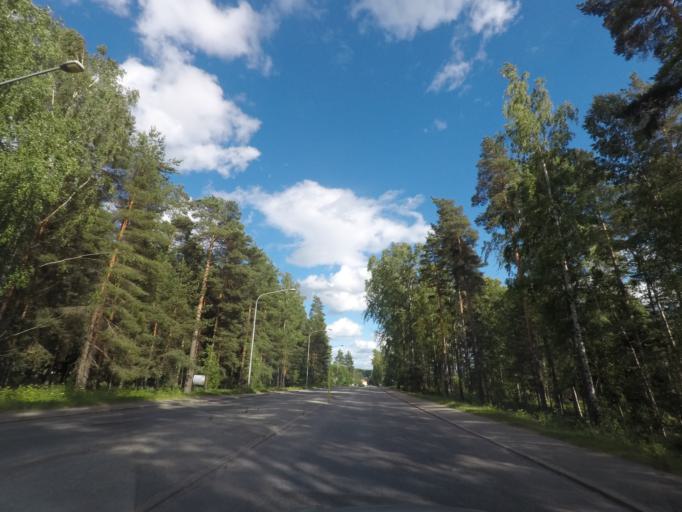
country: SE
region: OErebro
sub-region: Lindesbergs Kommun
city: Lindesberg
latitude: 59.6032
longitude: 15.2096
